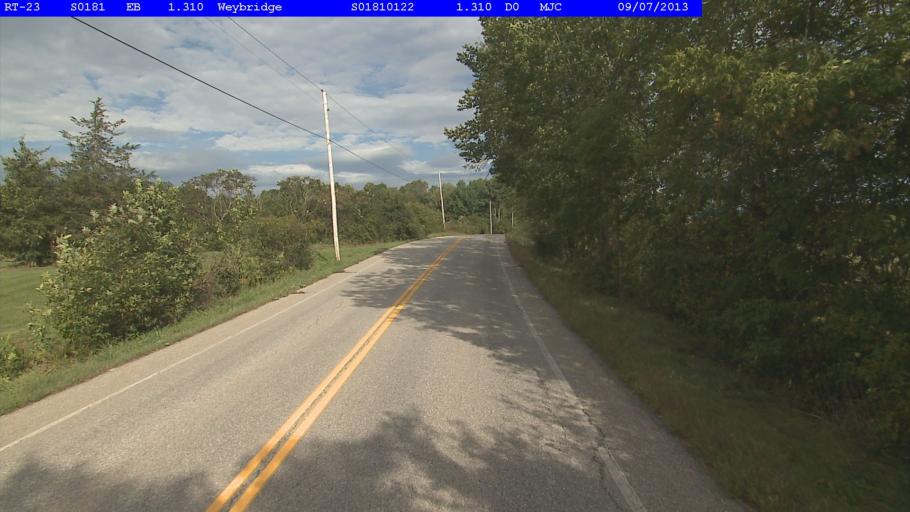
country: US
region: Vermont
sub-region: Addison County
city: Middlebury (village)
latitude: 44.0312
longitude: -73.2023
